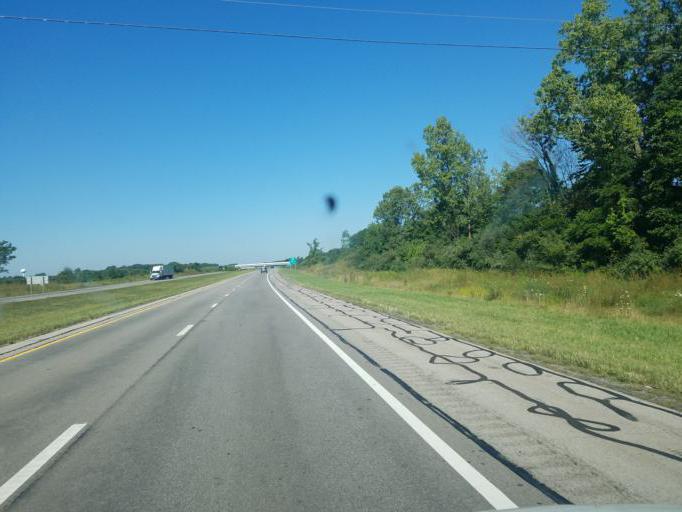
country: US
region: Ohio
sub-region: Crawford County
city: Galion
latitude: 40.7611
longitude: -82.7749
